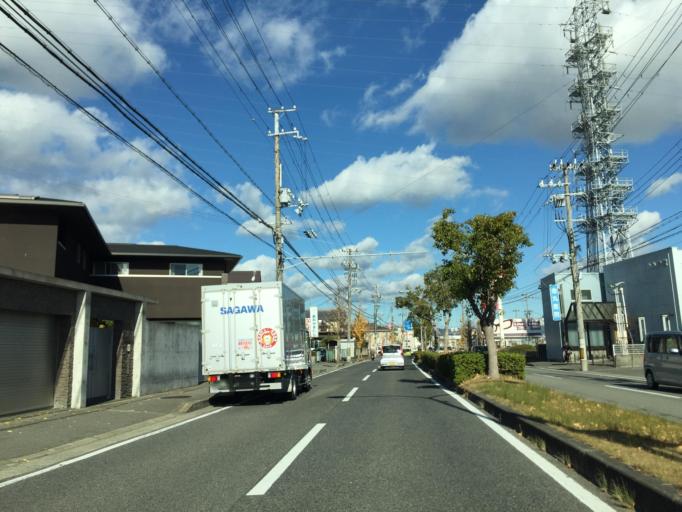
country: JP
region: Wakayama
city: Wakayama-shi
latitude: 34.1989
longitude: 135.1778
